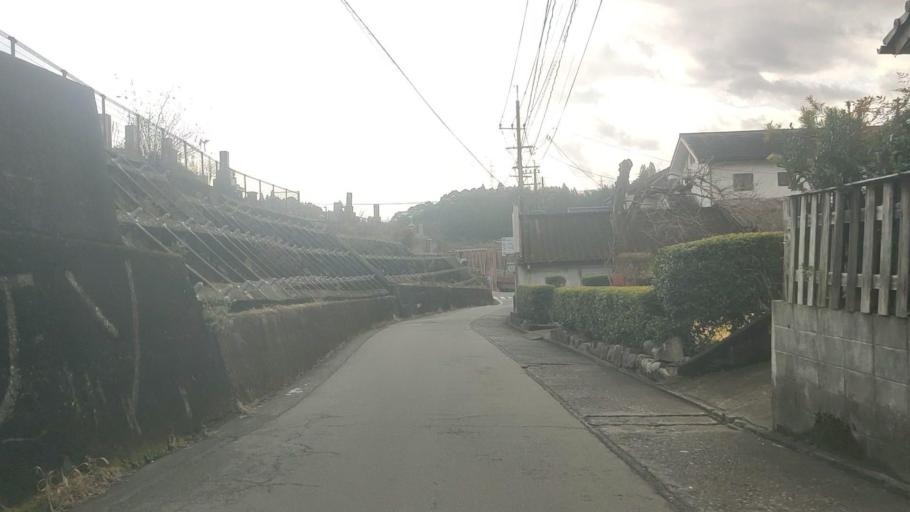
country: JP
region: Kumamoto
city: Hitoyoshi
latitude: 32.2170
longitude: 130.7718
